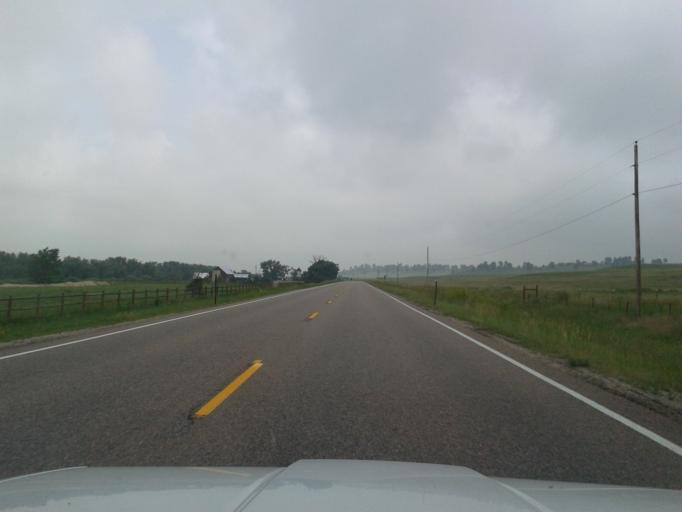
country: US
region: Colorado
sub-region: Elbert County
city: Elizabeth
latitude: 39.2408
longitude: -104.6969
